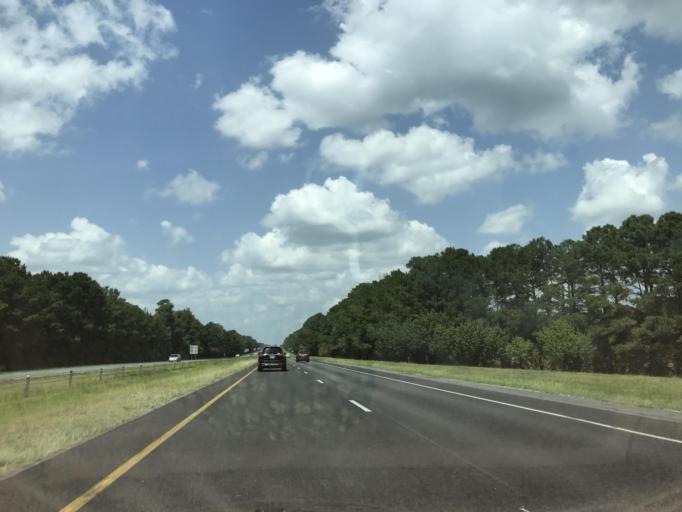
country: US
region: North Carolina
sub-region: Duplin County
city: Wallace
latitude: 34.7566
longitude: -77.9519
